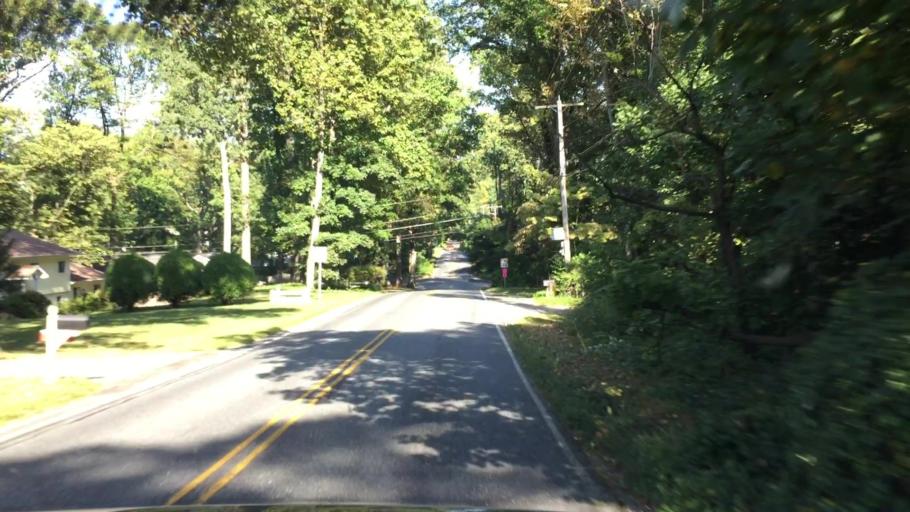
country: US
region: Maryland
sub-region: Anne Arundel County
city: Arnold
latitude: 39.0503
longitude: -76.4784
